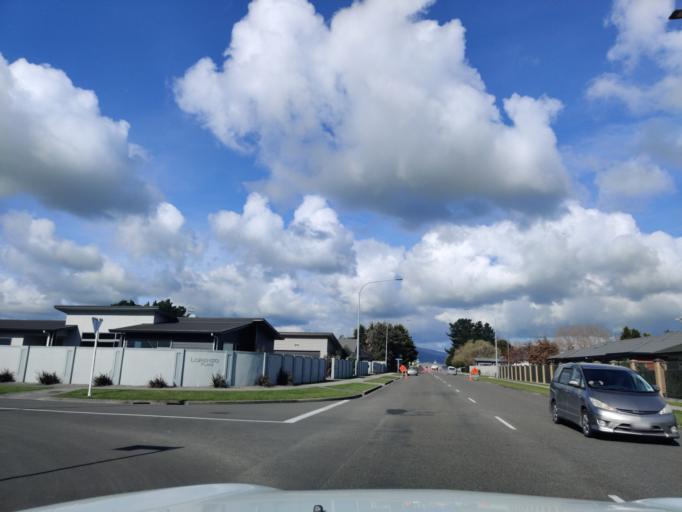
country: NZ
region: Manawatu-Wanganui
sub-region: Palmerston North City
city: Palmerston North
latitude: -40.3266
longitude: 175.6629
